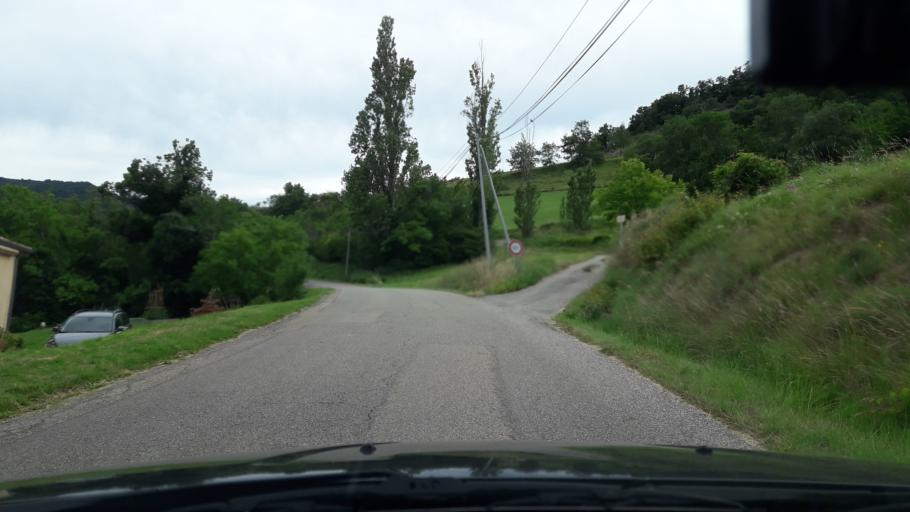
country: FR
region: Rhone-Alpes
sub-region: Departement de l'Ardeche
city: Alissas
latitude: 44.6927
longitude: 4.6358
